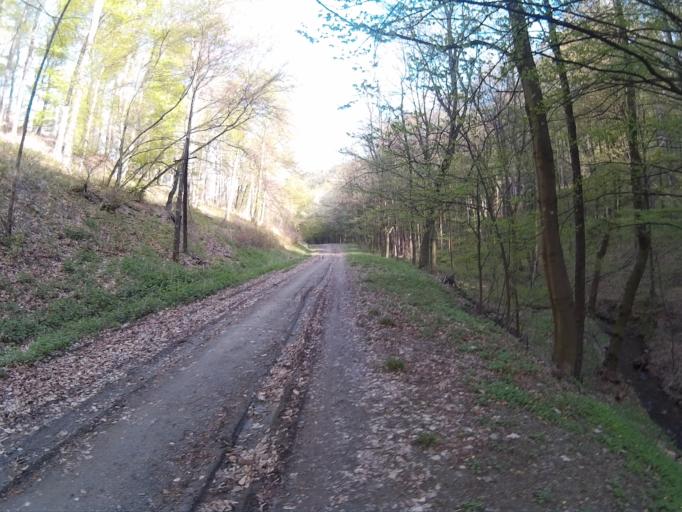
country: AT
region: Burgenland
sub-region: Politischer Bezirk Oberwart
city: Rechnitz
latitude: 47.3377
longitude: 16.4741
